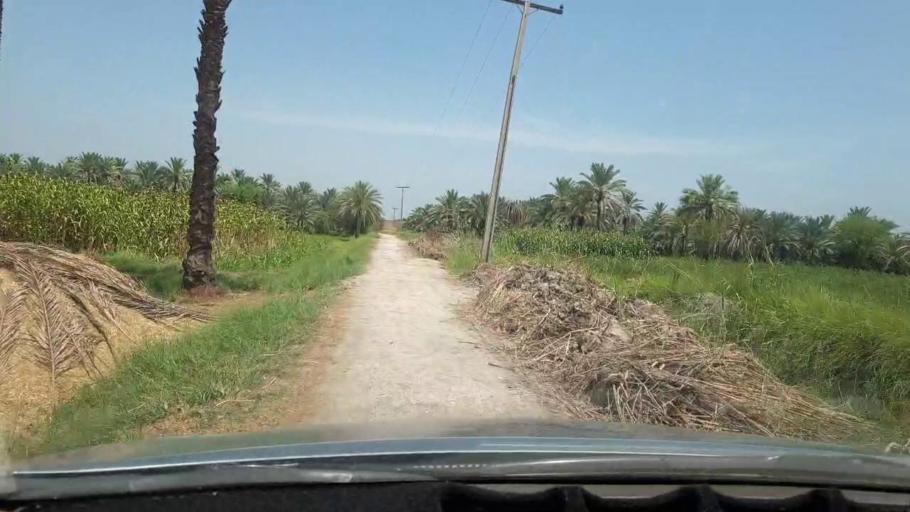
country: PK
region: Sindh
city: Khairpur
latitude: 27.4894
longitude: 68.7698
